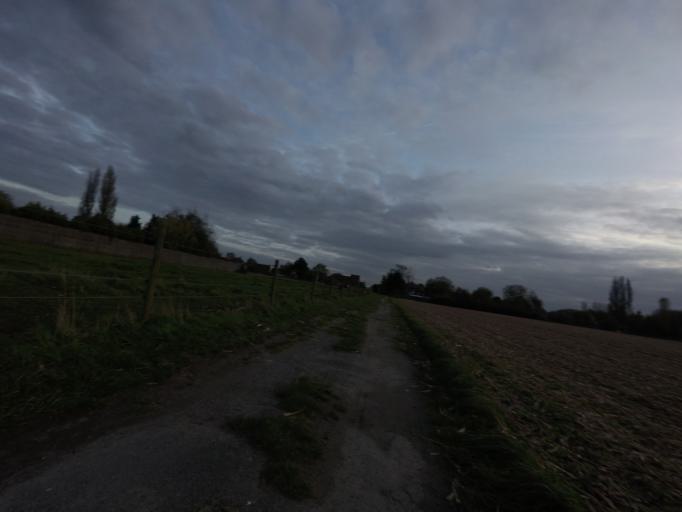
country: BE
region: Flanders
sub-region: Provincie Vlaams-Brabant
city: Steenokkerzeel
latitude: 50.9228
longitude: 4.5312
